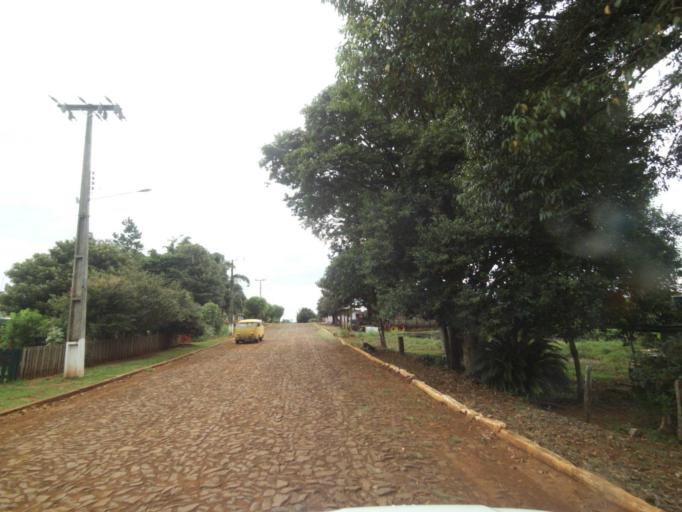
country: BR
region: Parana
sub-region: Guaraniacu
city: Guaraniacu
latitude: -24.9212
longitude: -52.9376
